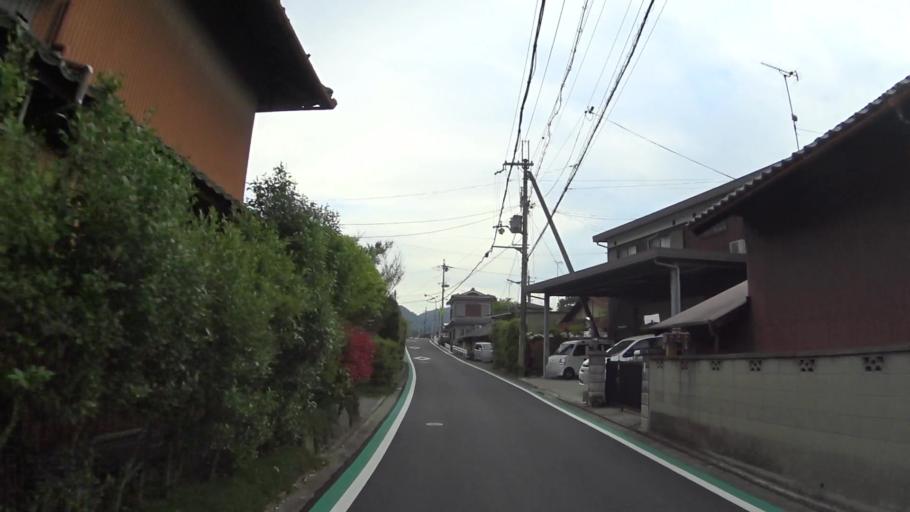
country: JP
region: Kyoto
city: Kameoka
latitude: 35.0092
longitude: 135.5477
